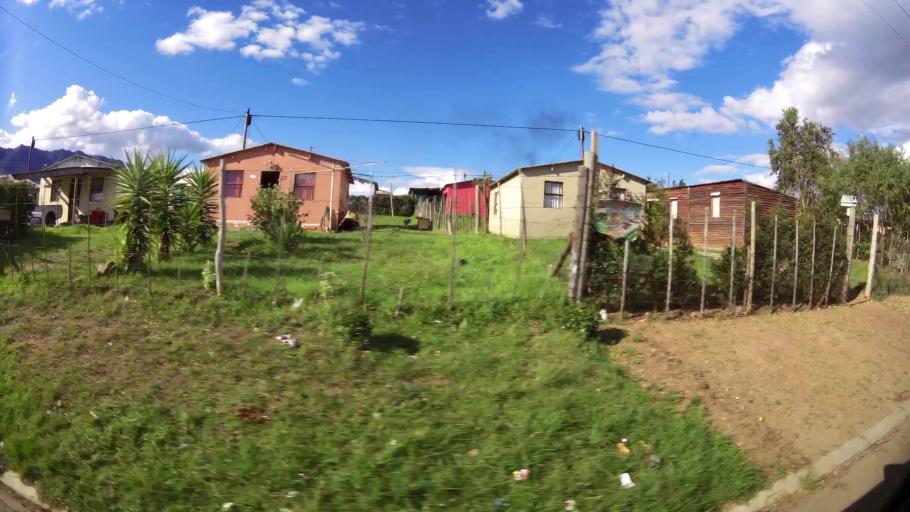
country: ZA
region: Western Cape
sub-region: Overberg District Municipality
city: Swellendam
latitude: -34.0336
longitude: 20.4513
